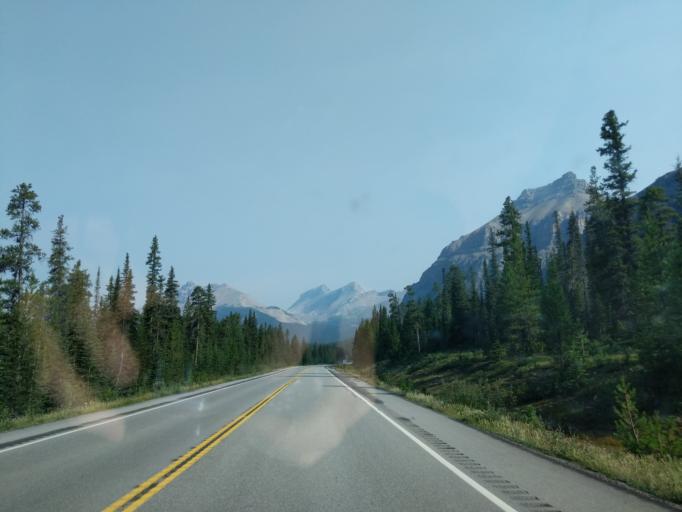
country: CA
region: Alberta
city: Lake Louise
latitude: 51.6115
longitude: -116.3141
